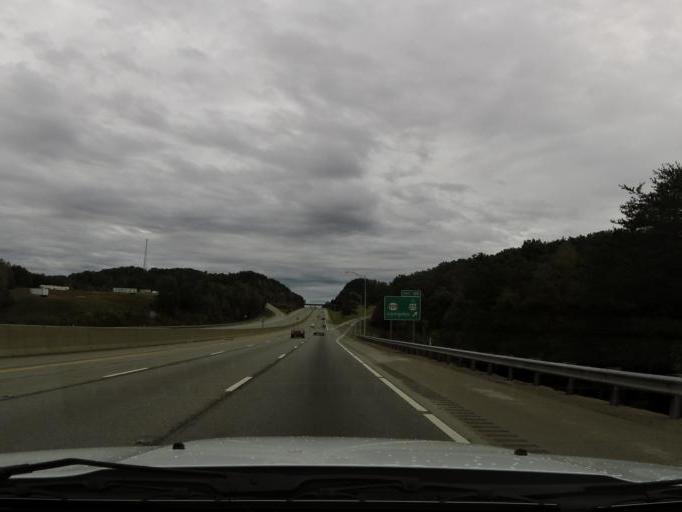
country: US
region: Kentucky
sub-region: Laurel County
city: London
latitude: 37.2223
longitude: -84.2080
